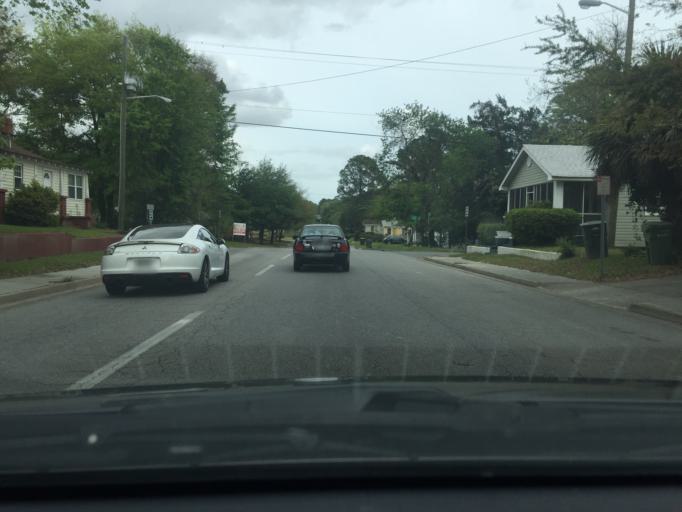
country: US
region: Georgia
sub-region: Chatham County
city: Savannah
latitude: 32.0567
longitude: -81.0768
